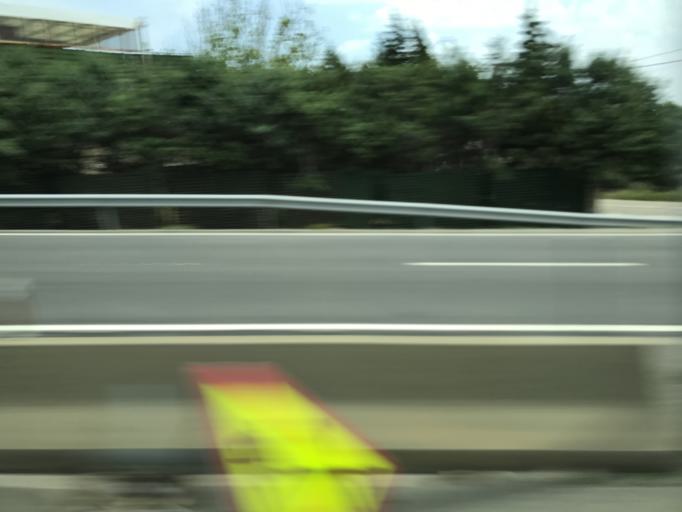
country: ES
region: Madrid
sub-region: Provincia de Madrid
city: Buitrago del Lozoya
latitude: 40.9312
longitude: -3.6244
